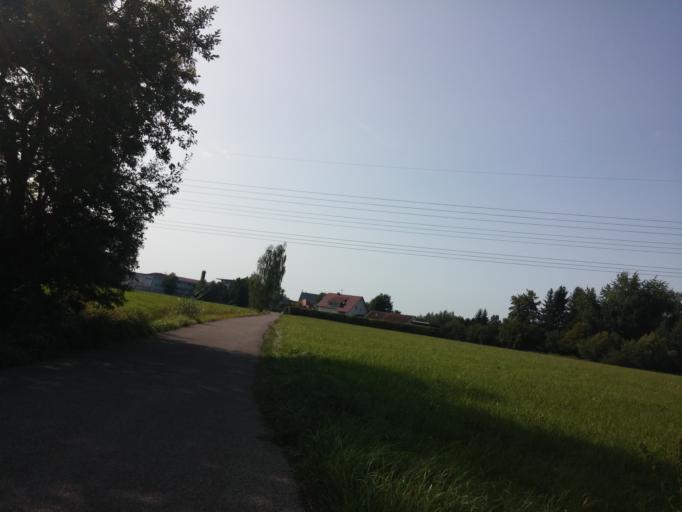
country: DE
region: Bavaria
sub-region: Swabia
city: Memmingen
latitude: 47.9737
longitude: 10.1991
